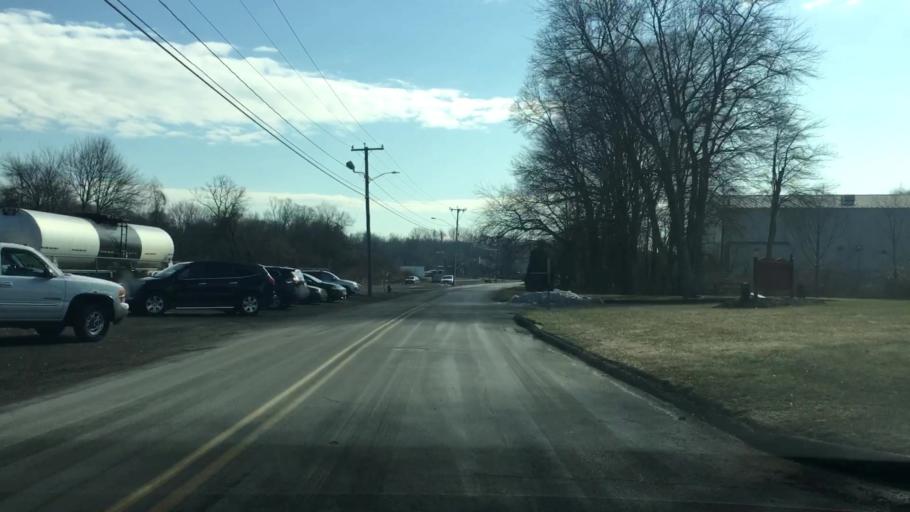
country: US
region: Connecticut
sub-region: Hartford County
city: Kensington
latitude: 41.6157
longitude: -72.7099
